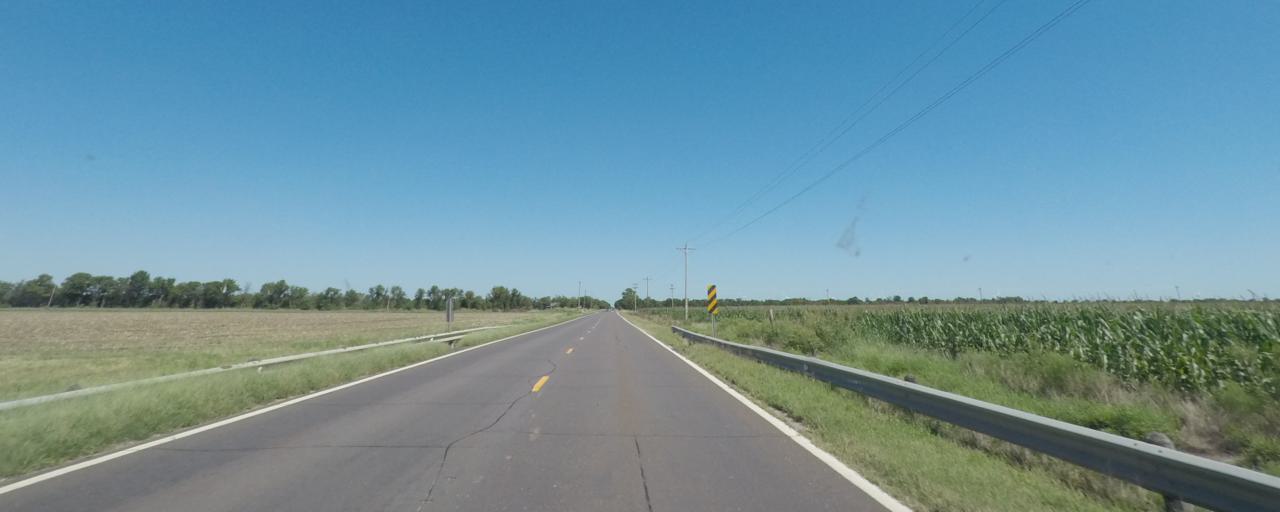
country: US
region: Kansas
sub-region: Sumner County
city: Wellington
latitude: 37.0980
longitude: -97.4015
